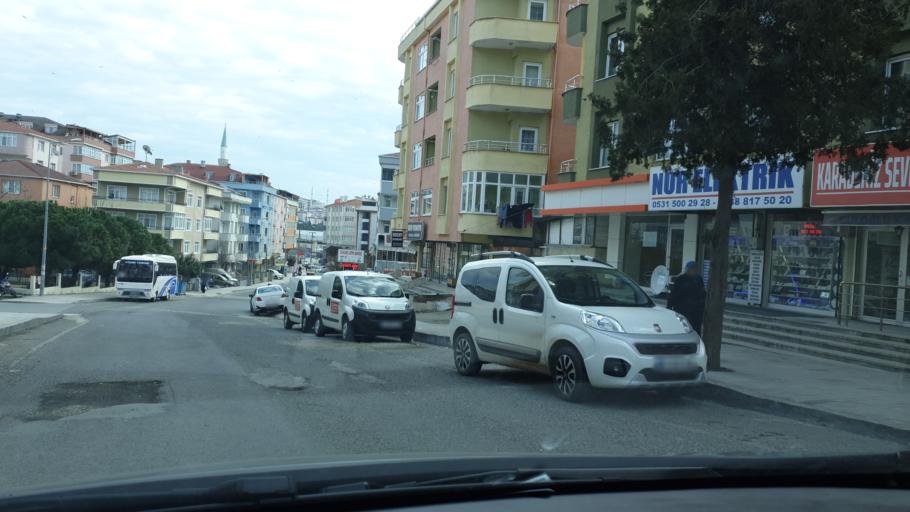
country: TR
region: Tekirdag
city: Cerkezkoey
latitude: 41.2835
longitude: 27.9949
